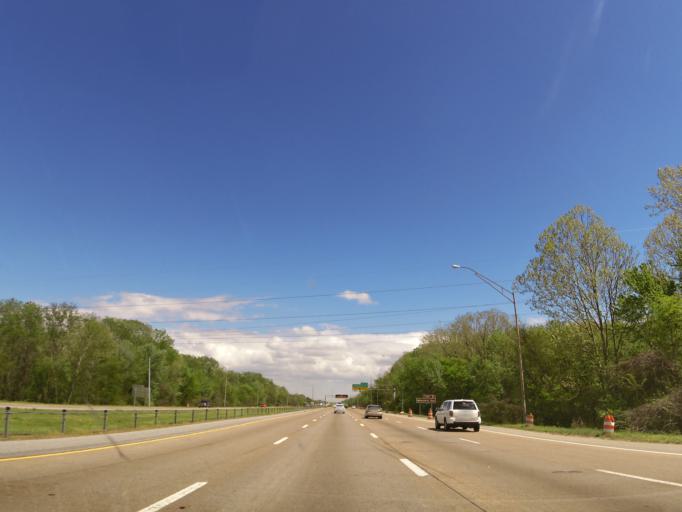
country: US
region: Tennessee
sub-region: Shelby County
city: Memphis
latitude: 35.1923
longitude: -89.9912
